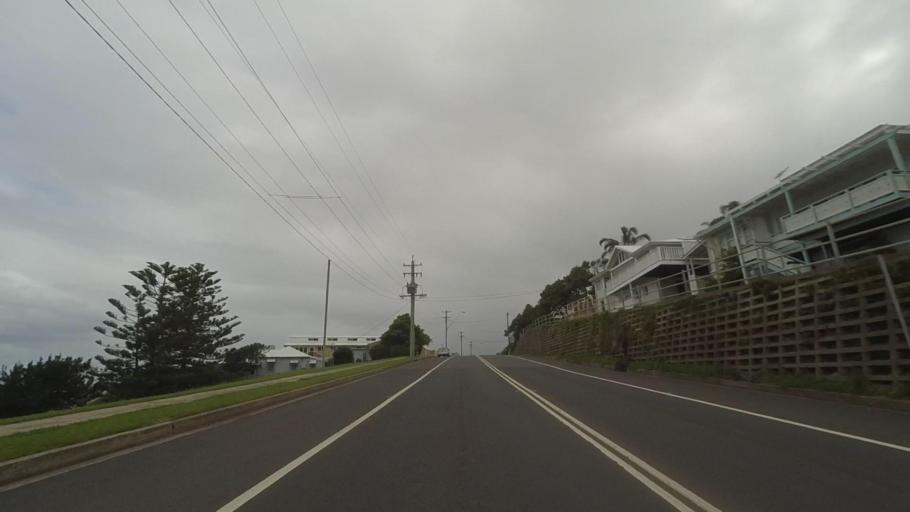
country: AU
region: New South Wales
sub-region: Wollongong
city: Bulli
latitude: -34.3094
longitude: 150.9326
